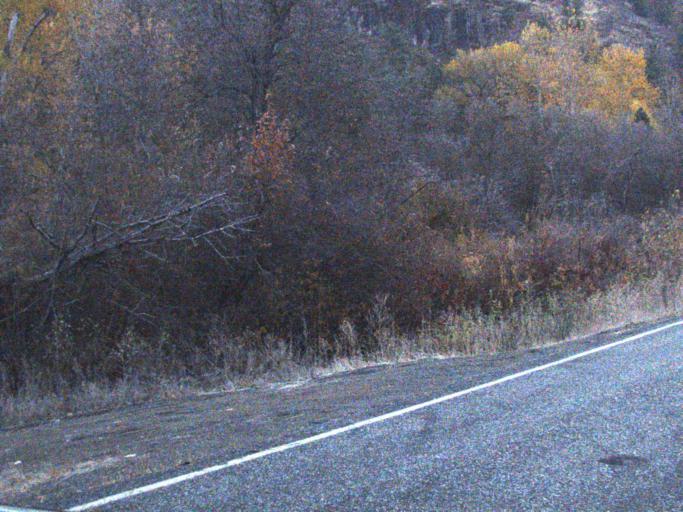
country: US
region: Washington
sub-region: Ferry County
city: Republic
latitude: 48.4330
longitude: -118.7327
